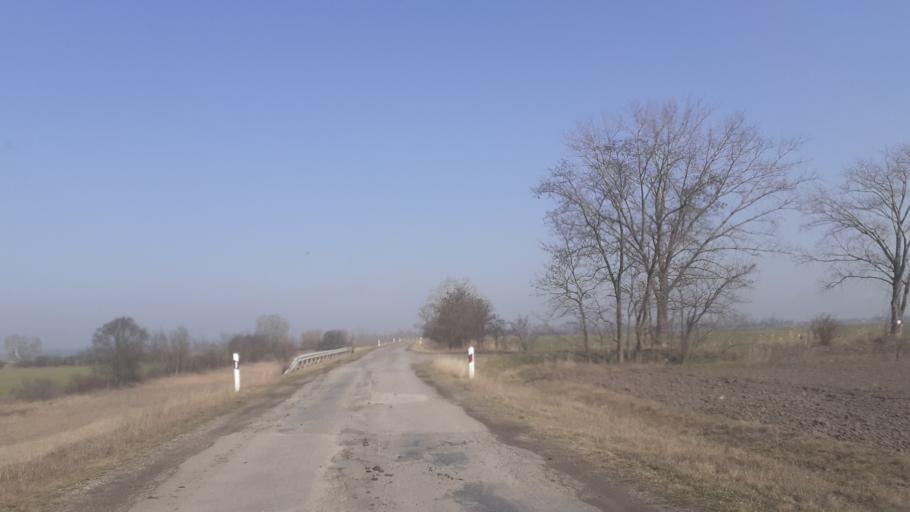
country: HU
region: Pest
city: Domsod
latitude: 47.0491
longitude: 18.9940
